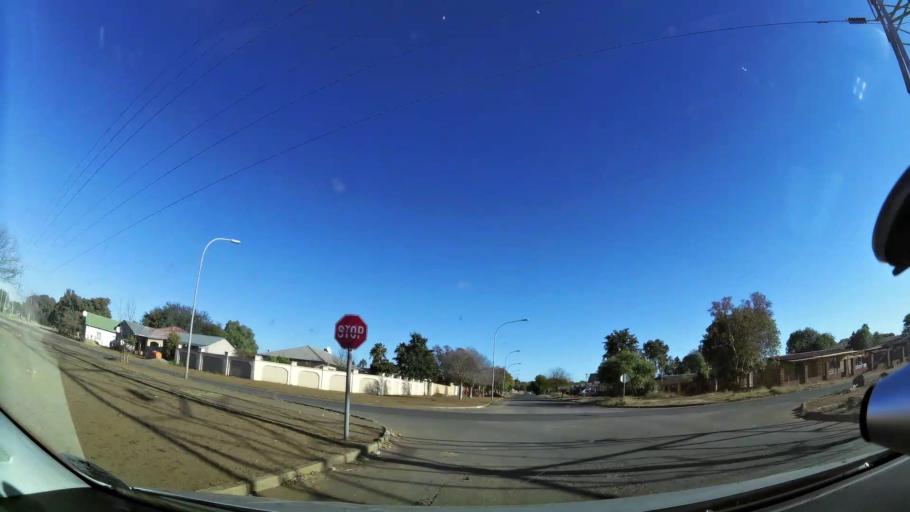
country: ZA
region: Northern Cape
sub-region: Frances Baard District Municipality
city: Kimberley
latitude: -28.7596
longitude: 24.7783
